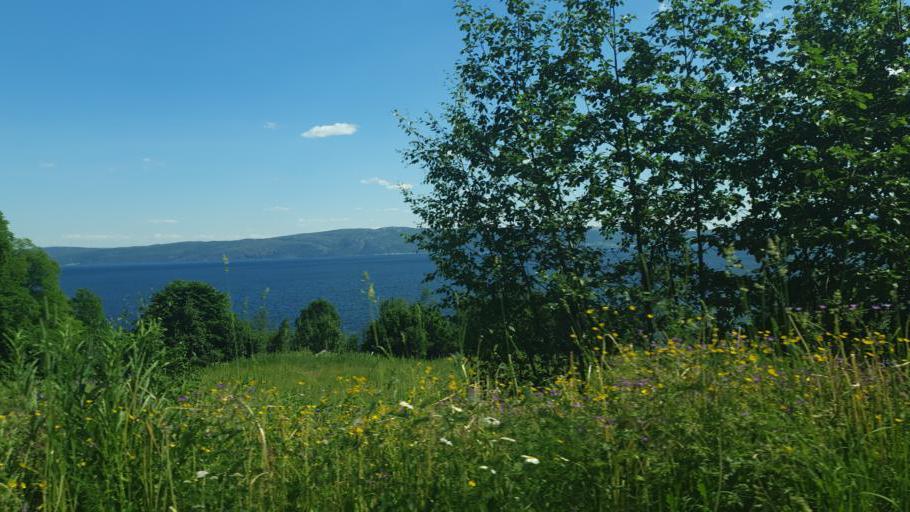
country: NO
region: Nord-Trondelag
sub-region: Frosta
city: Frosta
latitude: 63.7008
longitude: 10.7397
